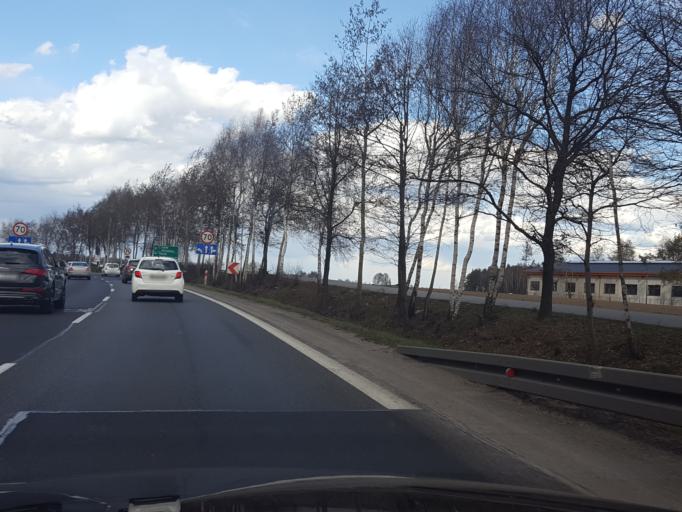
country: PL
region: Silesian Voivodeship
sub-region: Powiat pszczynski
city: Piasek
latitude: 50.0087
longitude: 18.9569
